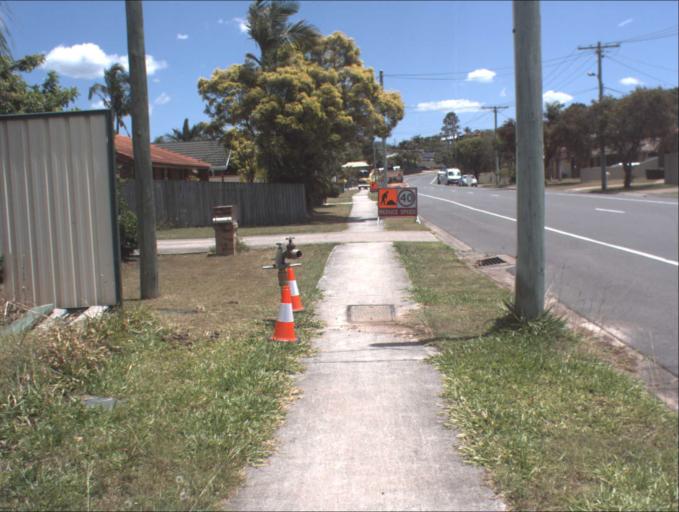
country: AU
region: Queensland
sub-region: Logan
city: Windaroo
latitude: -27.7355
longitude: 153.2100
